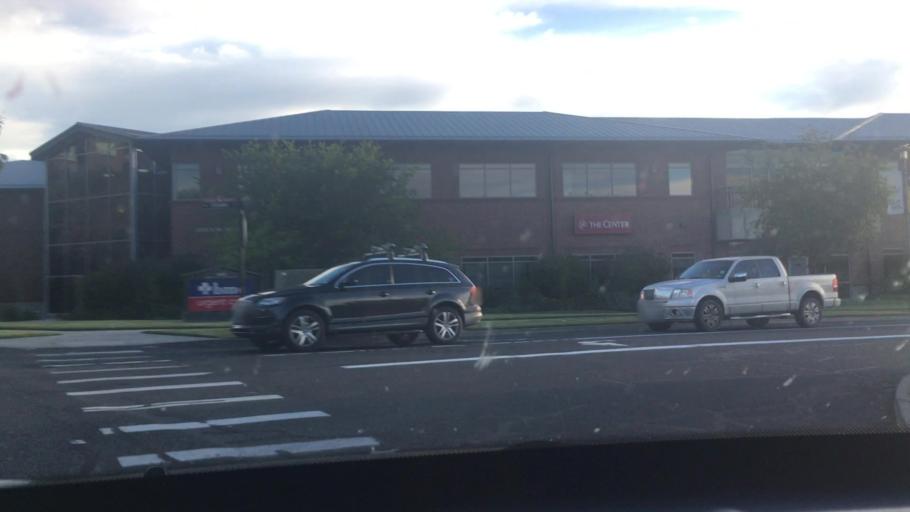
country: US
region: Oregon
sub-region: Deschutes County
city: Bend
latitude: 44.0424
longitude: -121.3144
